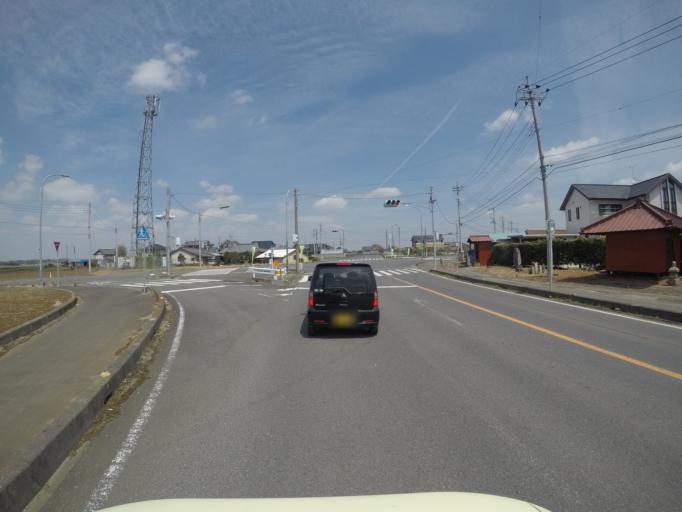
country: JP
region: Ibaraki
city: Shimodate
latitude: 36.3266
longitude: 139.9956
